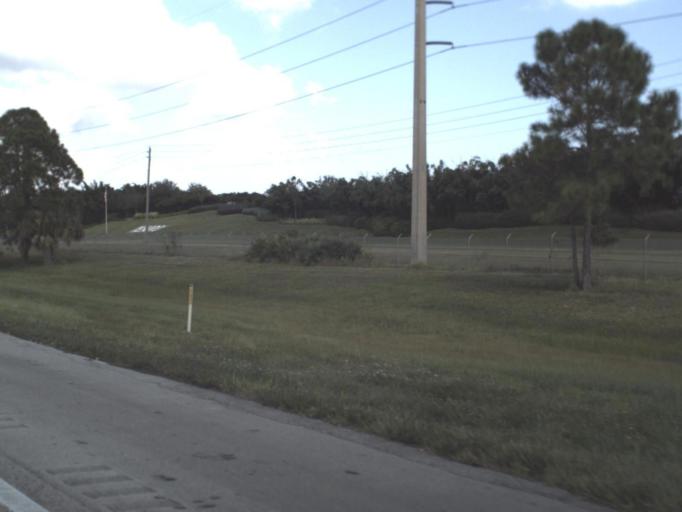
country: US
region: Florida
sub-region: Martin County
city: North River Shores
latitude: 27.2231
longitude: -80.3401
